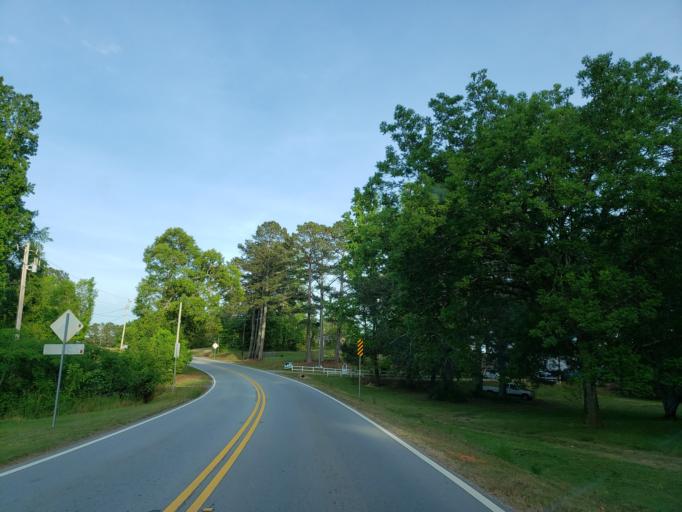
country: US
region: Georgia
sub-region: Carroll County
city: Carrollton
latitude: 33.5895
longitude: -85.1200
